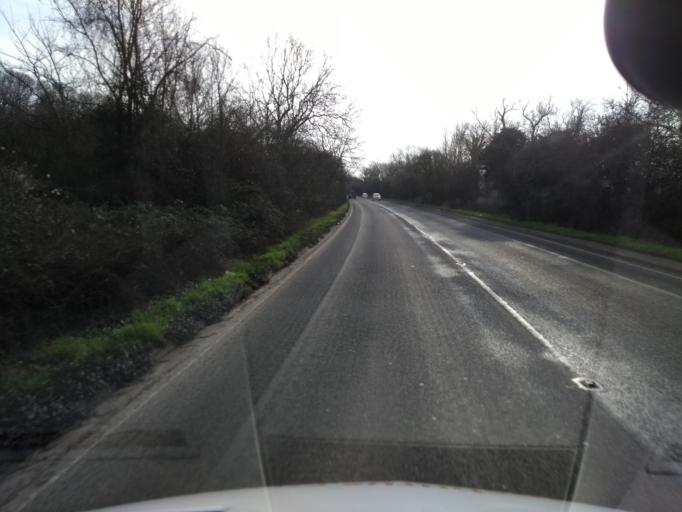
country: GB
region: England
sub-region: North Somerset
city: Bleadon
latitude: 51.3137
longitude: -2.9670
